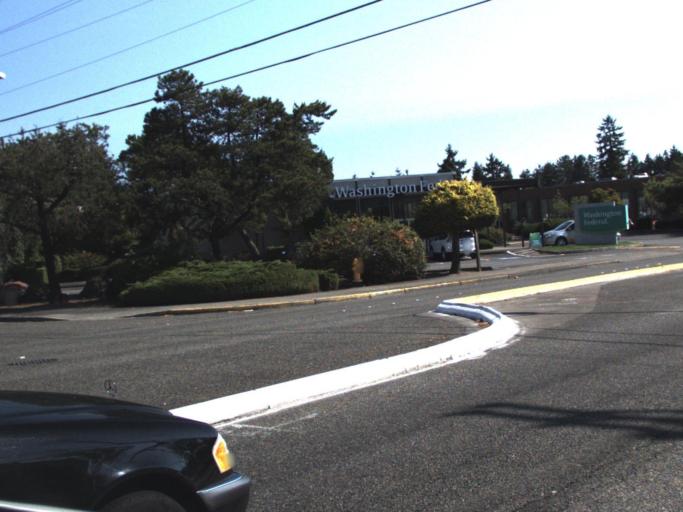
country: US
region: Washington
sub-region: Snohomish County
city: Lynnwood
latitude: 47.8212
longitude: -122.3121
